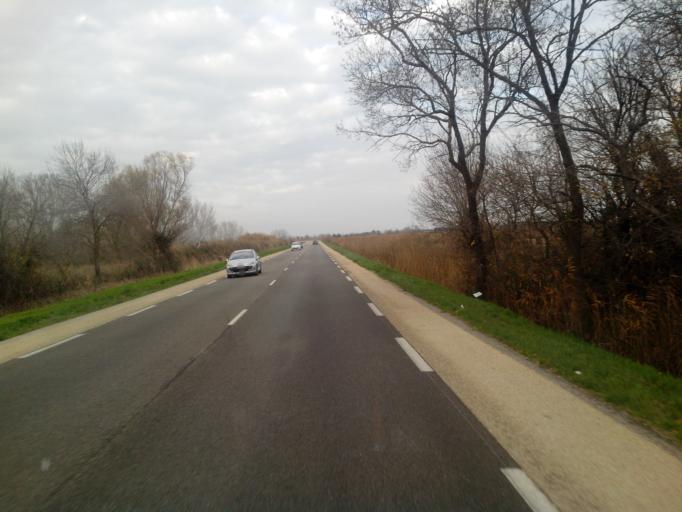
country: FR
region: Provence-Alpes-Cote d'Azur
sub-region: Departement des Bouches-du-Rhone
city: Saintes-Maries-de-la-Mer
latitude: 43.5629
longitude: 4.4197
